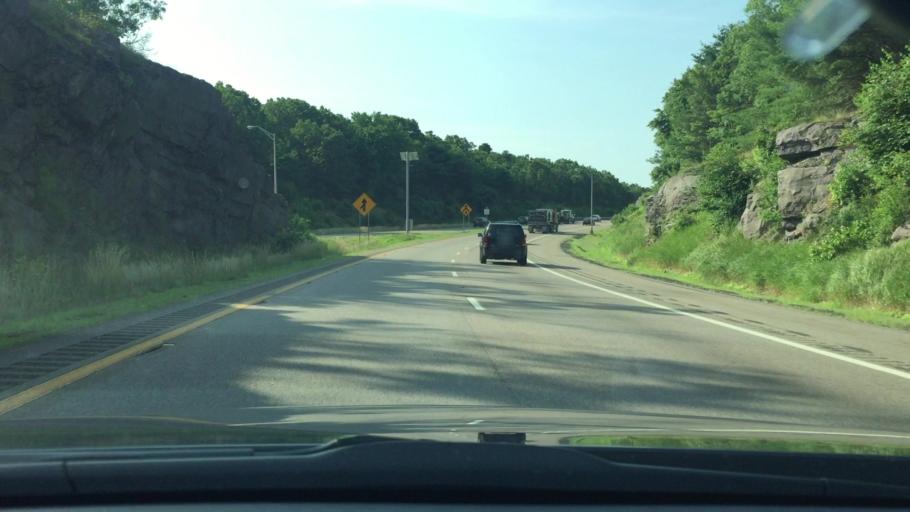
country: US
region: Massachusetts
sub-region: Norfolk County
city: Milton
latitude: 42.2001
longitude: -71.0797
